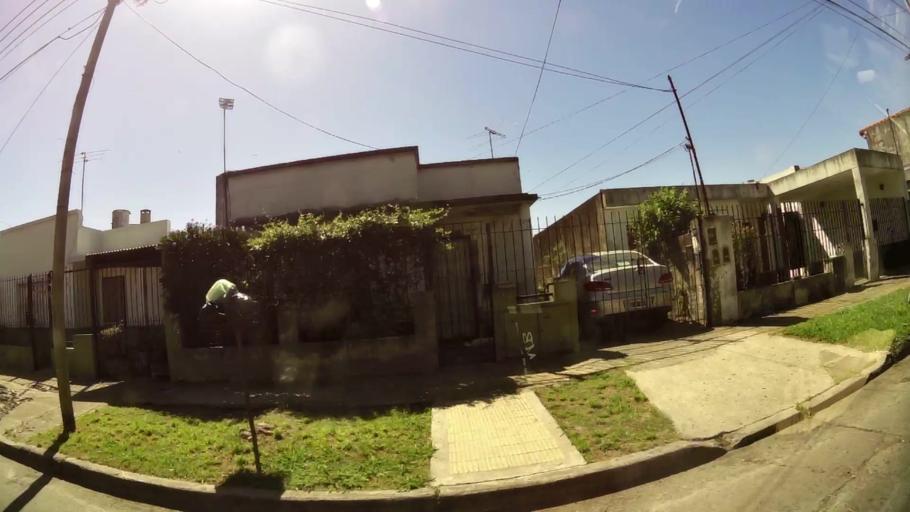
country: AR
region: Buenos Aires
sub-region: Partido de General San Martin
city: General San Martin
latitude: -34.5526
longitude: -58.5680
